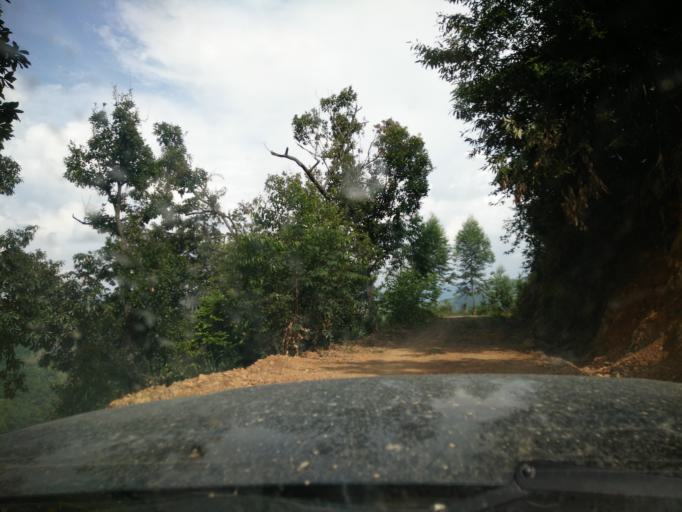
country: CN
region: Guangxi Zhuangzu Zizhiqu
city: Leli
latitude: 24.7642
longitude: 105.9039
